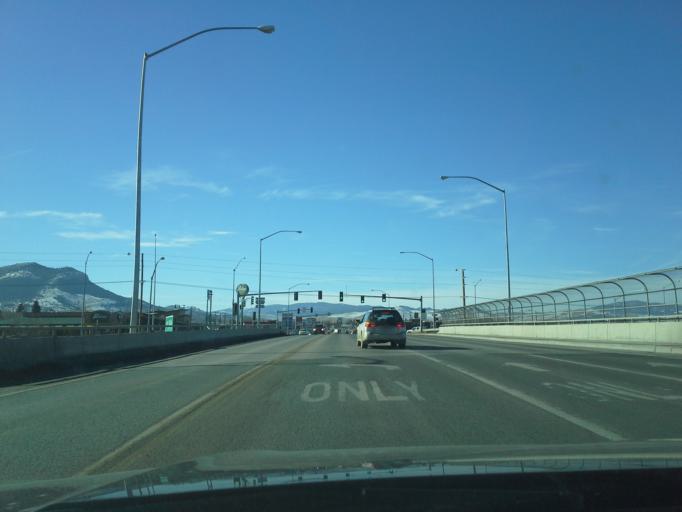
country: US
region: Montana
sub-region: Lewis and Clark County
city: Helena
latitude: 46.6068
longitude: -112.0072
